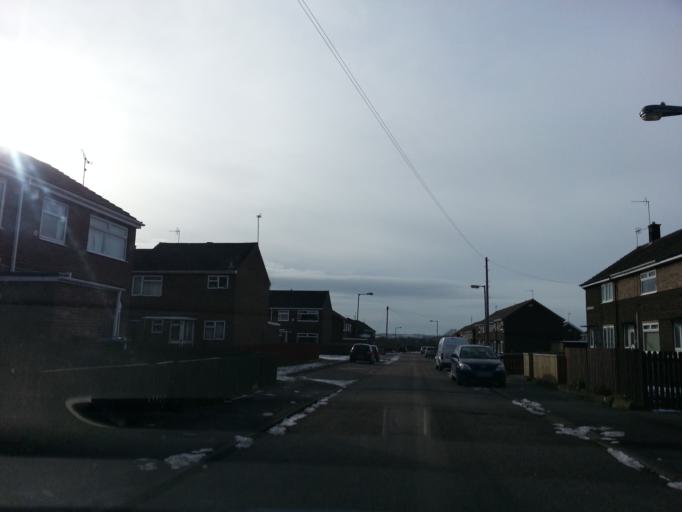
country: GB
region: England
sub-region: County Durham
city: Crook
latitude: 54.7073
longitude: -1.7421
